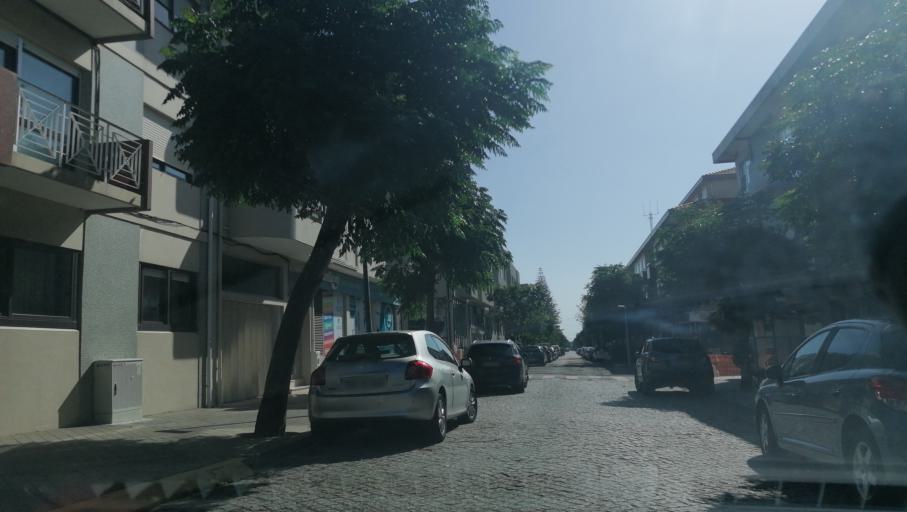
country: PT
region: Aveiro
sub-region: Espinho
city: Espinho
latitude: 41.0089
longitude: -8.6352
